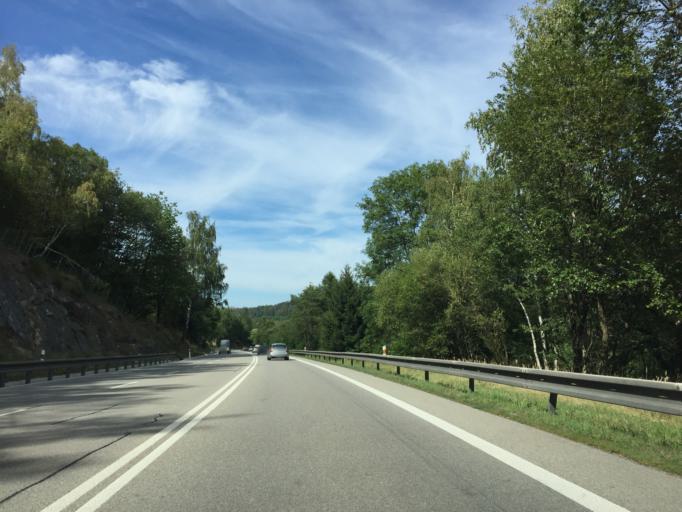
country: CZ
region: Central Bohemia
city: Votice
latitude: 49.6291
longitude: 14.6513
